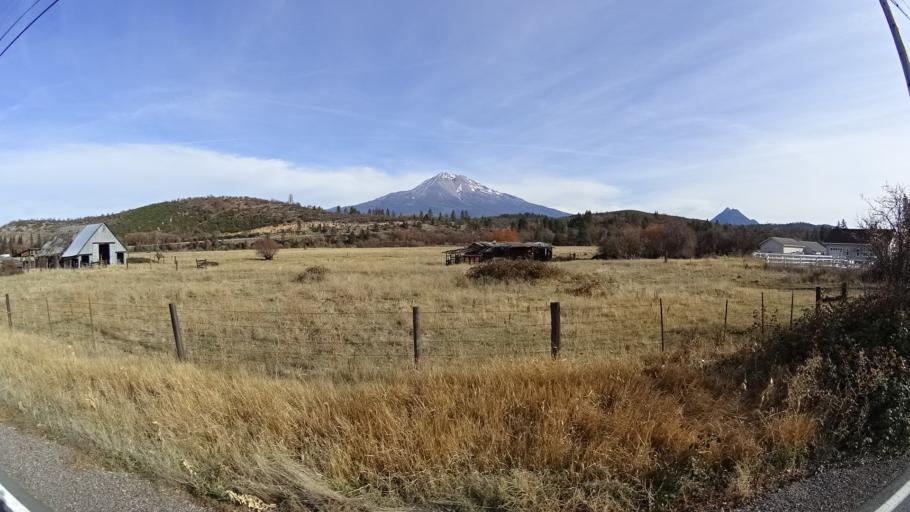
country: US
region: California
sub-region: Siskiyou County
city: Weed
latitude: 41.4333
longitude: -122.4366
